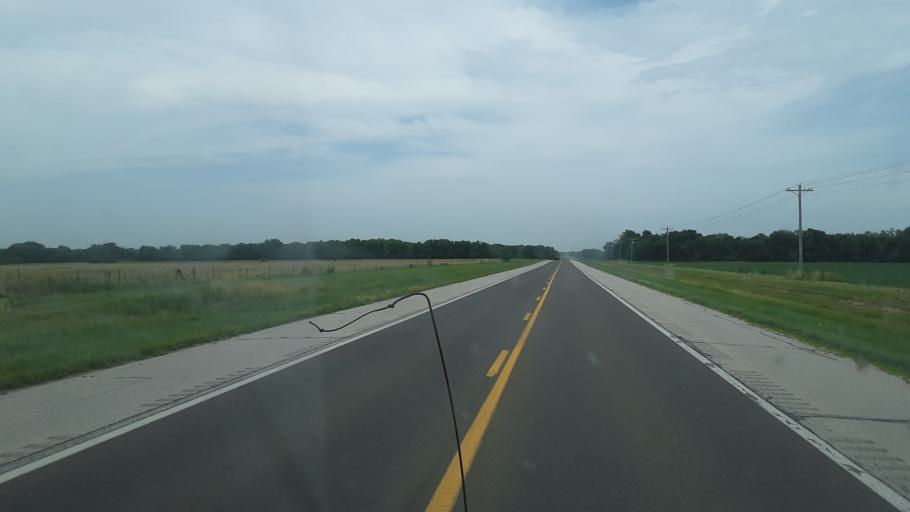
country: US
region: Kansas
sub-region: Allen County
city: Iola
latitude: 37.9222
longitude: -95.4605
